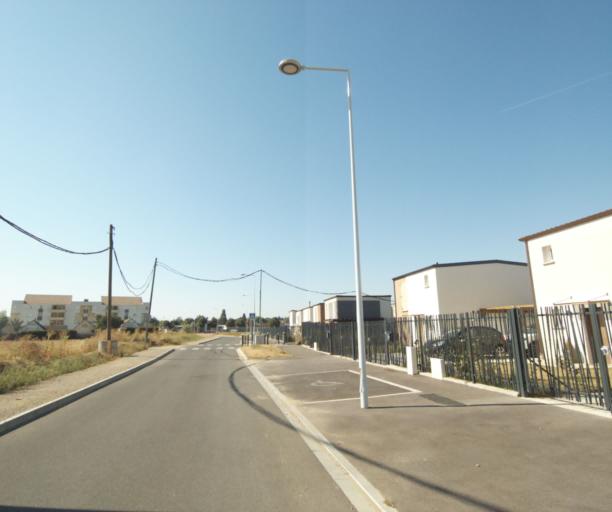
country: FR
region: Ile-de-France
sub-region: Departement de Seine-et-Marne
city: Moissy-Cramayel
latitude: 48.6341
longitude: 2.5867
